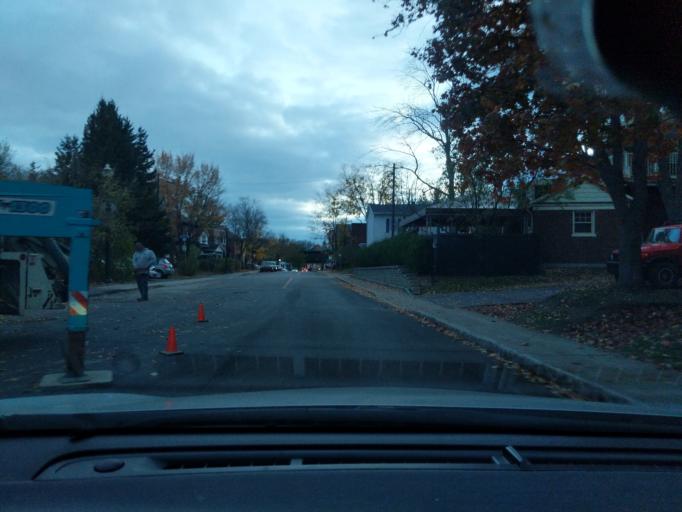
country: CA
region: Quebec
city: Quebec
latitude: 46.7811
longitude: -71.2484
